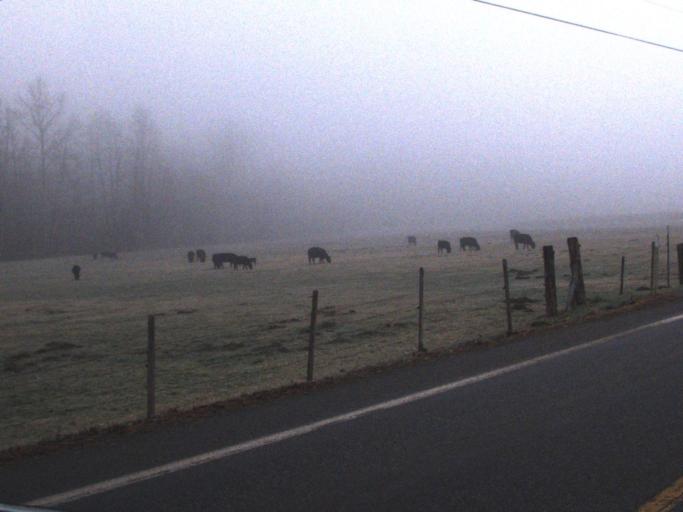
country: US
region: Washington
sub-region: Snohomish County
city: Darrington
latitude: 48.4958
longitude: -121.5380
